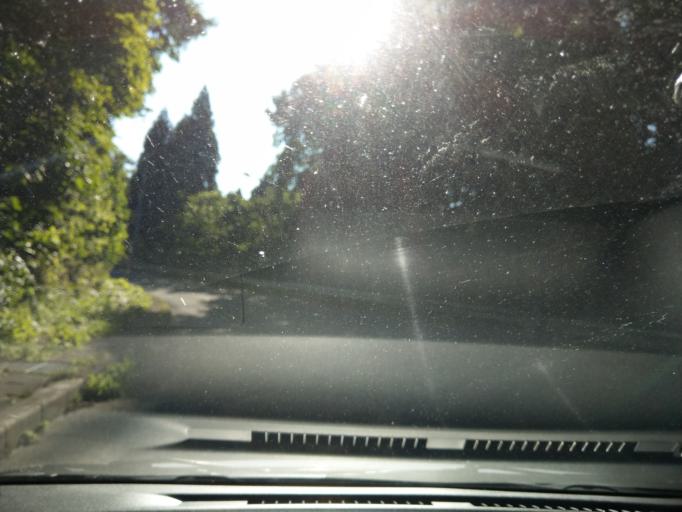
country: JP
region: Akita
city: Takanosu
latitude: 40.1686
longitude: 140.3956
